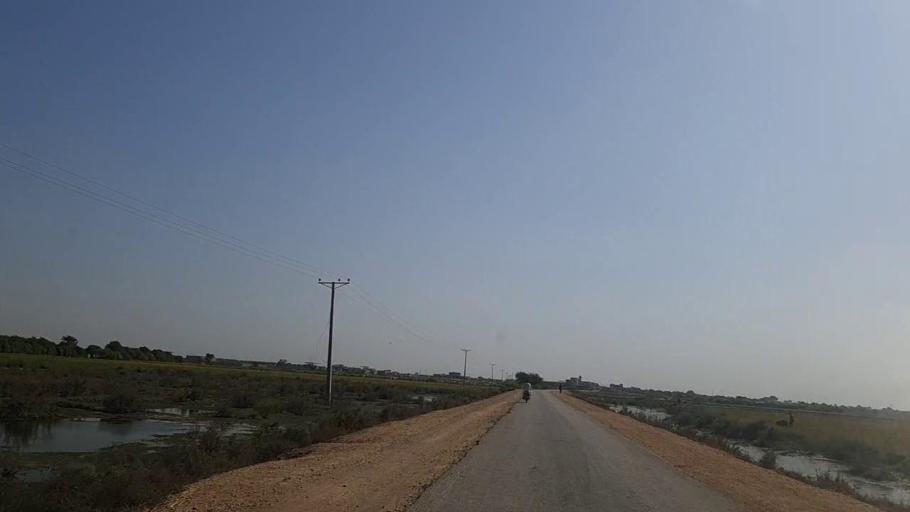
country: PK
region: Sindh
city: Mirpur Batoro
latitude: 24.6252
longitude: 68.2944
